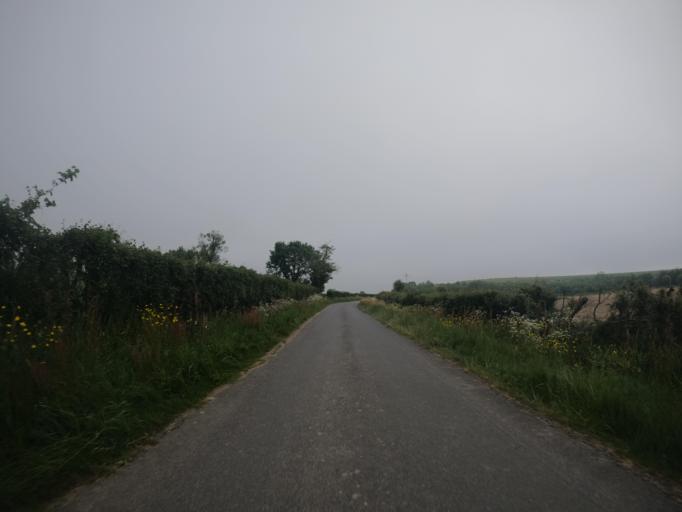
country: FR
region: Poitou-Charentes
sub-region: Departement des Deux-Sevres
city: Mauze-Thouarsais
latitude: 46.9058
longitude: -0.3288
